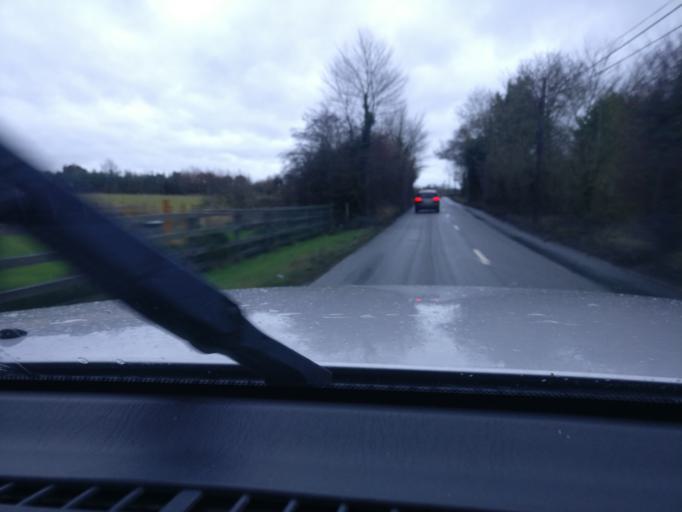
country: IE
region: Leinster
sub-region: An Mhi
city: Longwood
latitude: 53.4670
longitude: -6.9120
